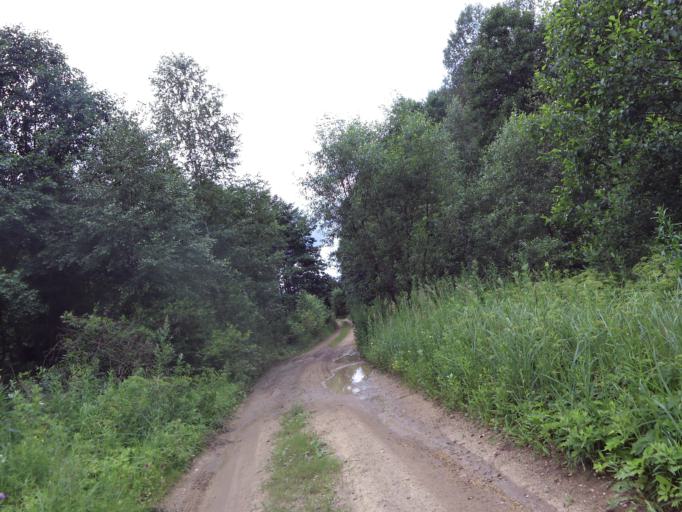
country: RU
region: Moskovskaya
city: Danki
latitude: 54.9436
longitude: 37.6862
